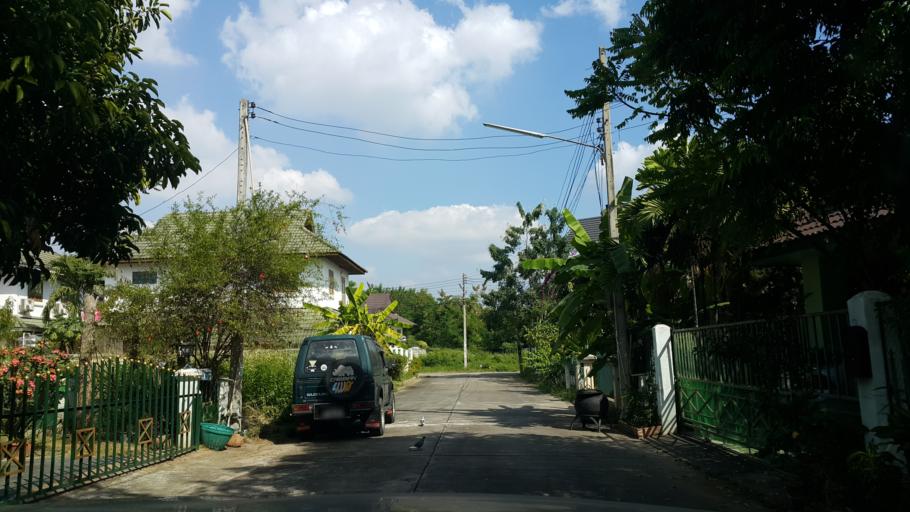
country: TH
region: Chiang Mai
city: Hang Dong
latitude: 18.7333
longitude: 98.9368
